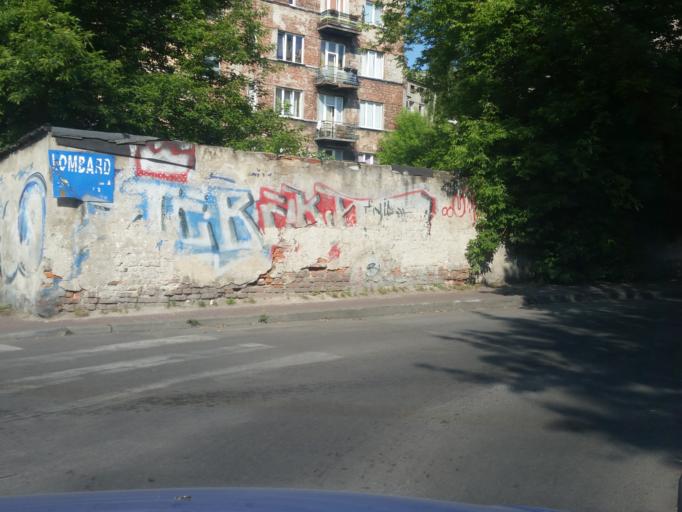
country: PL
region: Silesian Voivodeship
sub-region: Sosnowiec
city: Sosnowiec
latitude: 50.2740
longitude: 19.1217
